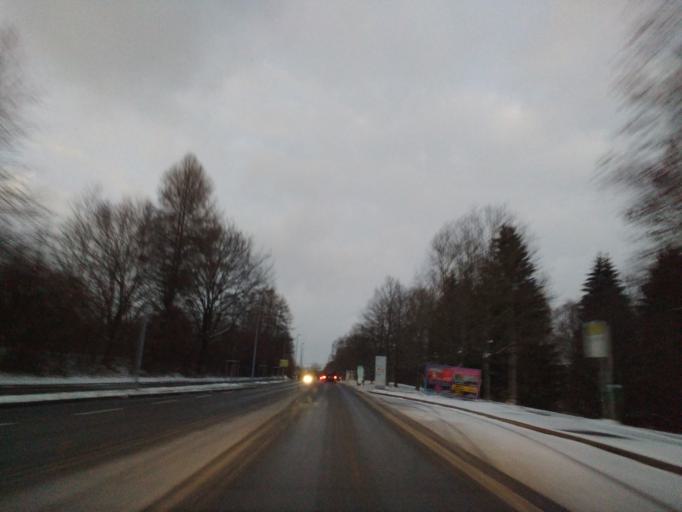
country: DE
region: Bavaria
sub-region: Swabia
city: Kempten (Allgaeu)
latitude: 47.7127
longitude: 10.2854
